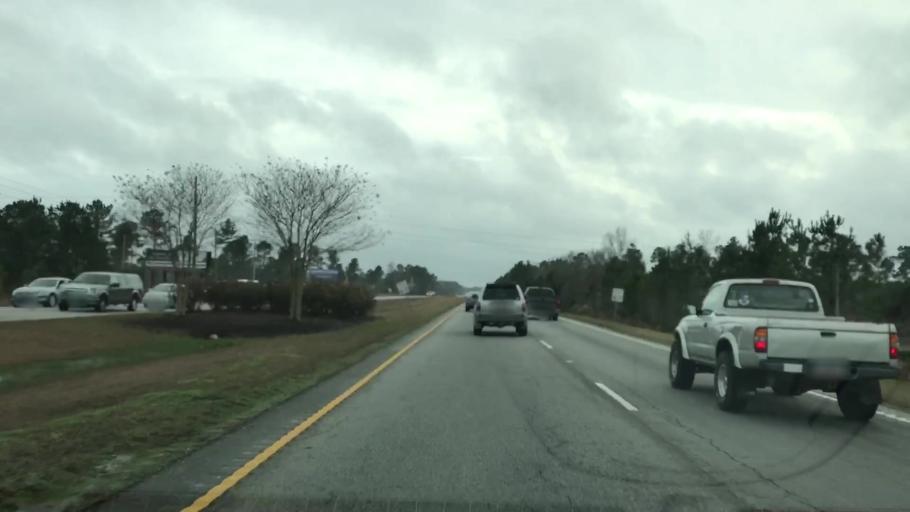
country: US
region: South Carolina
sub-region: Berkeley County
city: Moncks Corner
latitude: 33.0908
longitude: -80.0315
